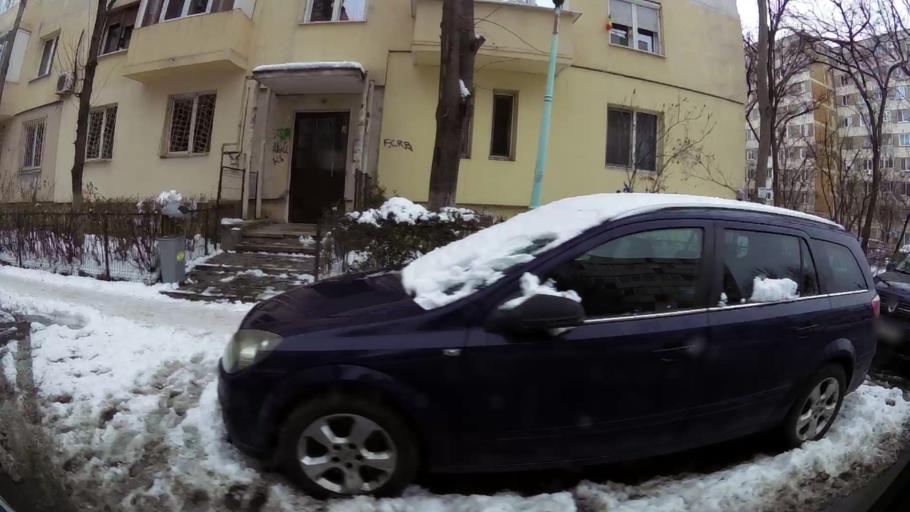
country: RO
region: Ilfov
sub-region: Comuna Popesti-Leordeni
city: Popesti-Leordeni
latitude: 44.3862
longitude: 26.1334
